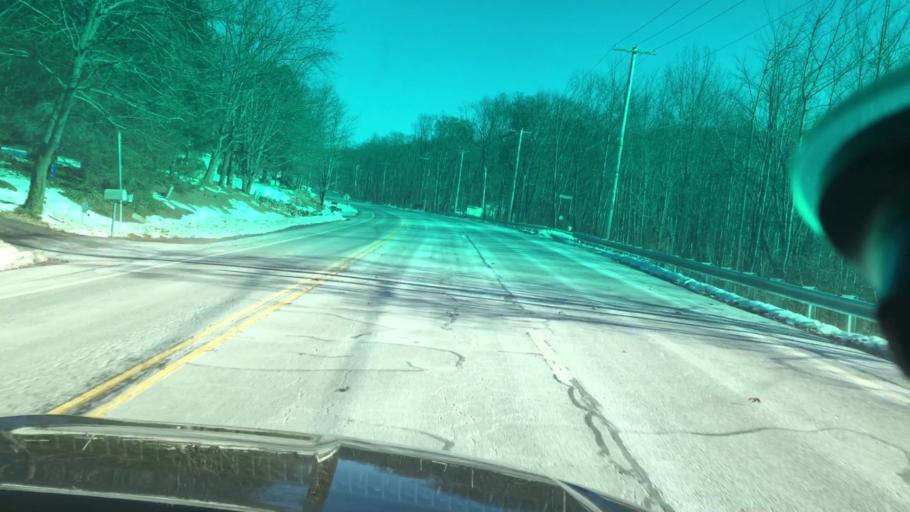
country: US
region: Pennsylvania
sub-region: Luzerne County
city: Oakdale
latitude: 41.0180
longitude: -75.9501
